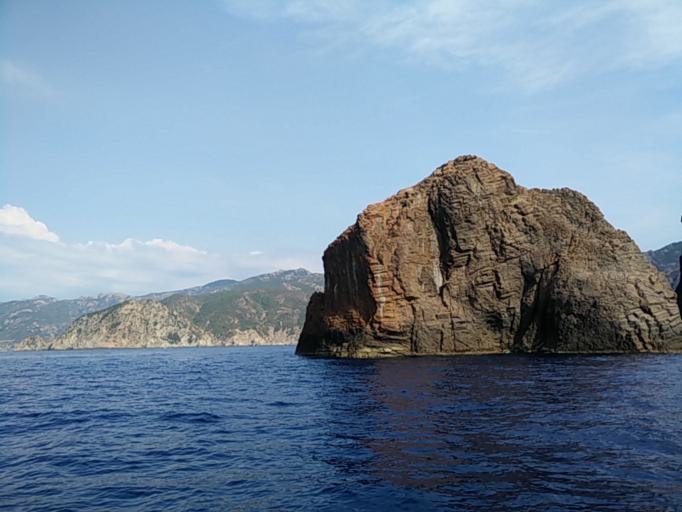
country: FR
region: Corsica
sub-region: Departement de la Corse-du-Sud
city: Cargese
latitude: 42.3802
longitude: 8.5494
